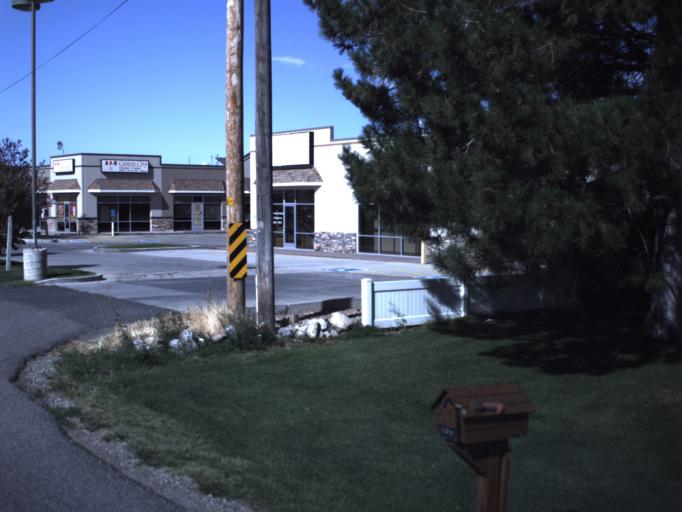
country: US
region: Utah
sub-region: Tooele County
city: Grantsville
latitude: 40.5986
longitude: -112.4260
